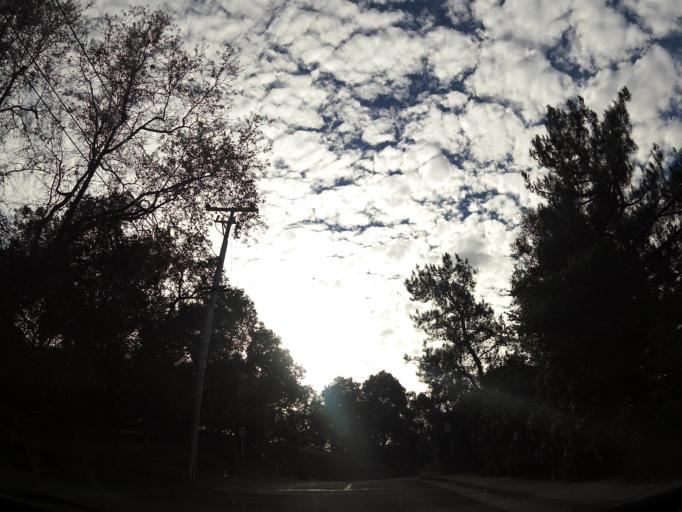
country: US
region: California
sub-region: Santa Clara County
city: Seven Trees
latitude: 37.1950
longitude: -121.8365
